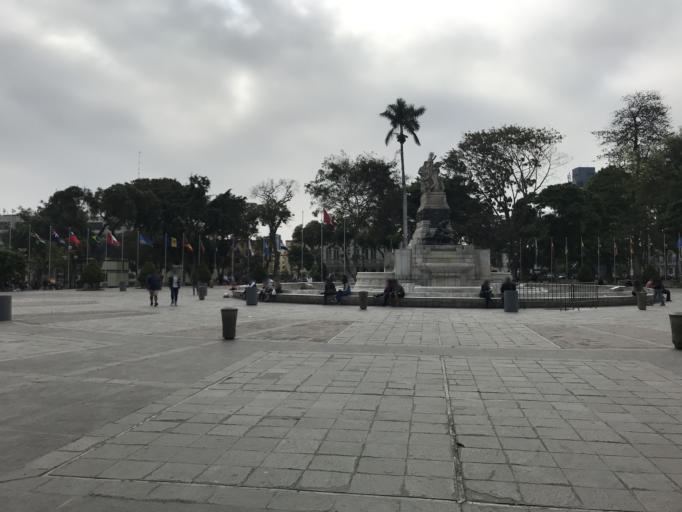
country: PE
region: Lima
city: Lima
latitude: -12.0621
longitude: -77.0362
